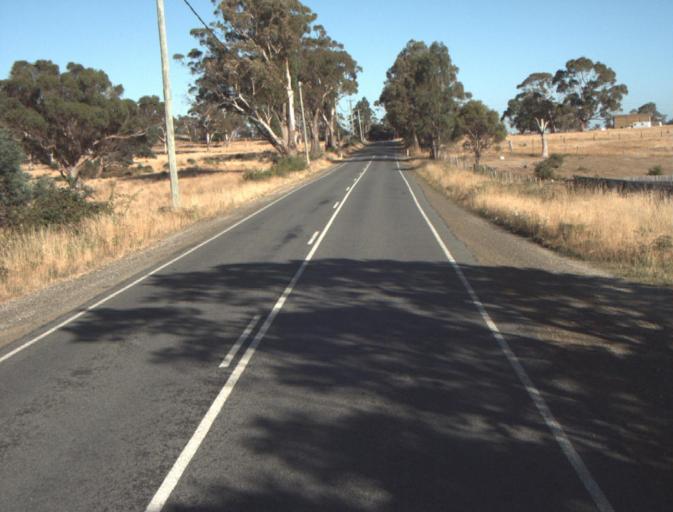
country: AU
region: Tasmania
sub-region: Launceston
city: Newstead
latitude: -41.4459
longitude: 147.2416
